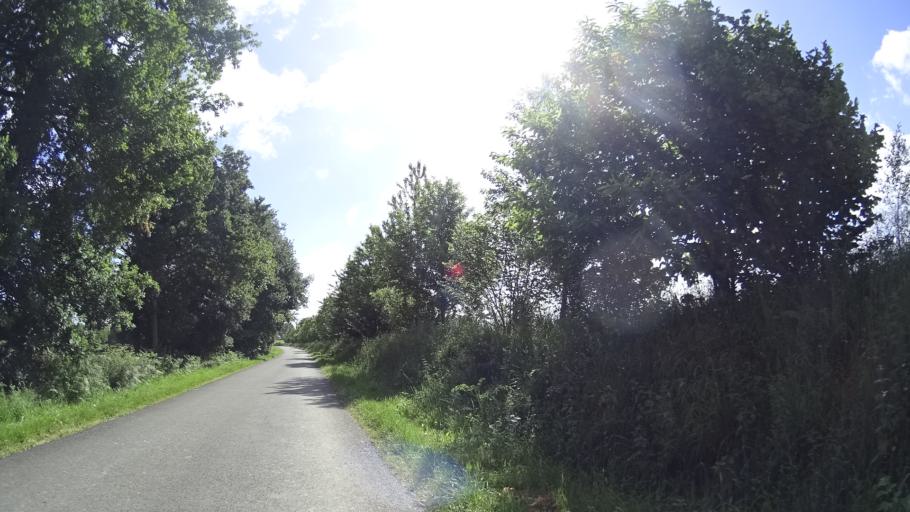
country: FR
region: Brittany
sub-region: Departement d'Ille-et-Vilaine
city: Melesse
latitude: 48.2078
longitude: -1.7115
